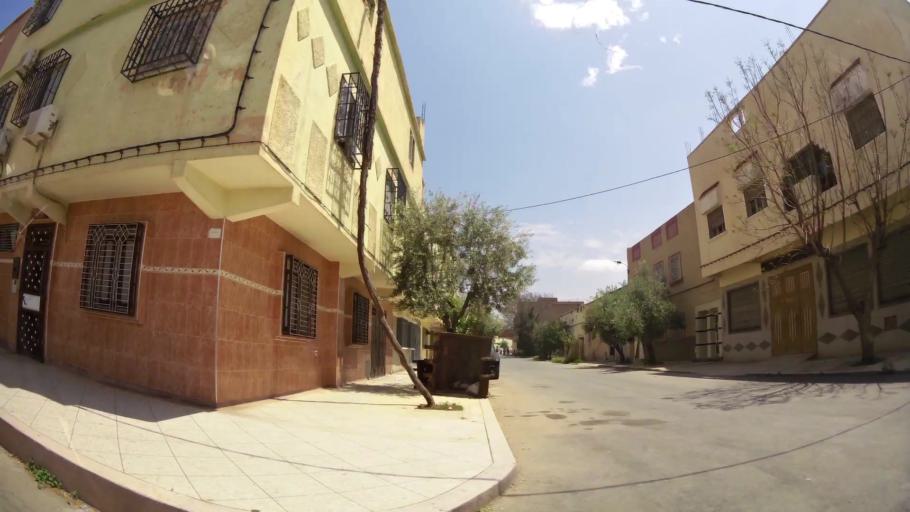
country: MA
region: Oriental
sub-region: Oujda-Angad
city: Oujda
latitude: 34.6832
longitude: -1.8887
